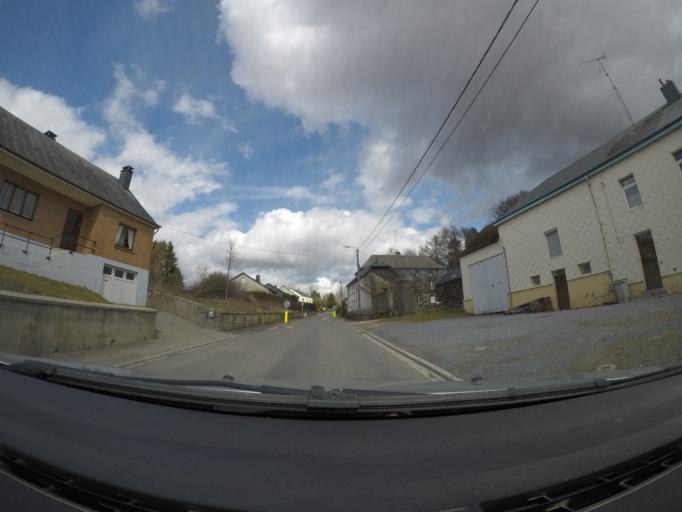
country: BE
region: Wallonia
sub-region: Province du Luxembourg
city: Leglise
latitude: 49.7697
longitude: 5.5222
